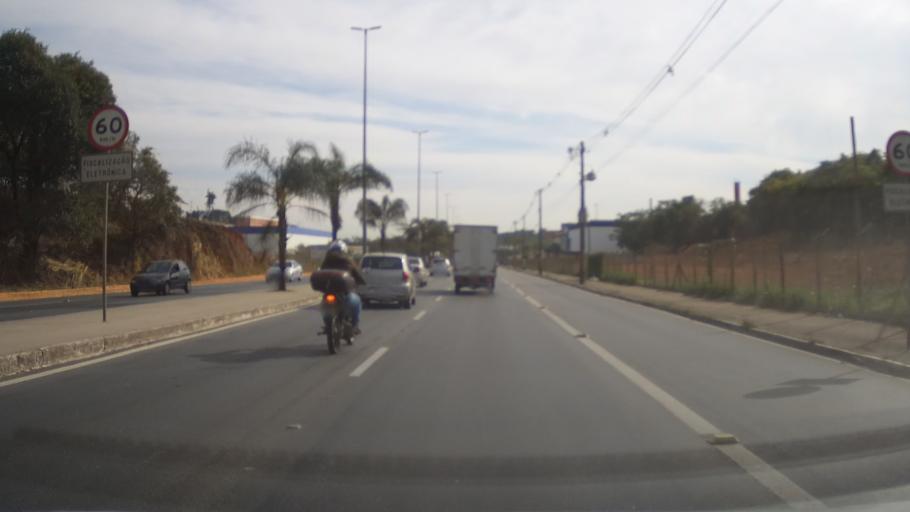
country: BR
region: Minas Gerais
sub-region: Contagem
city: Contagem
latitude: -19.9139
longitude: -44.0529
